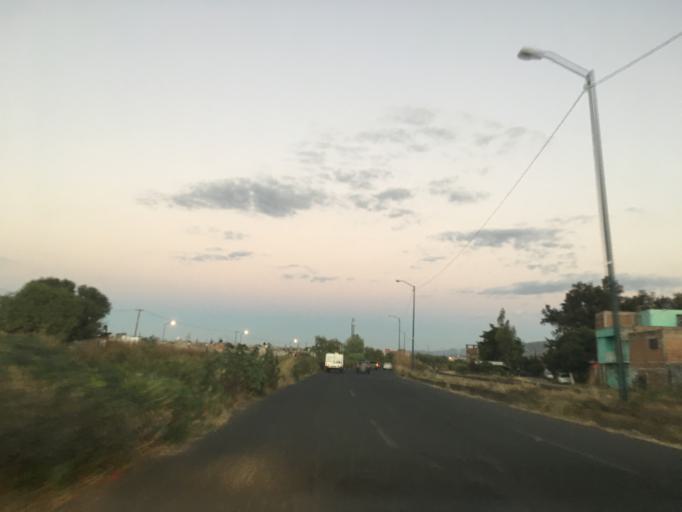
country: MX
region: Michoacan
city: Morelia
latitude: 19.7142
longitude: -101.2062
